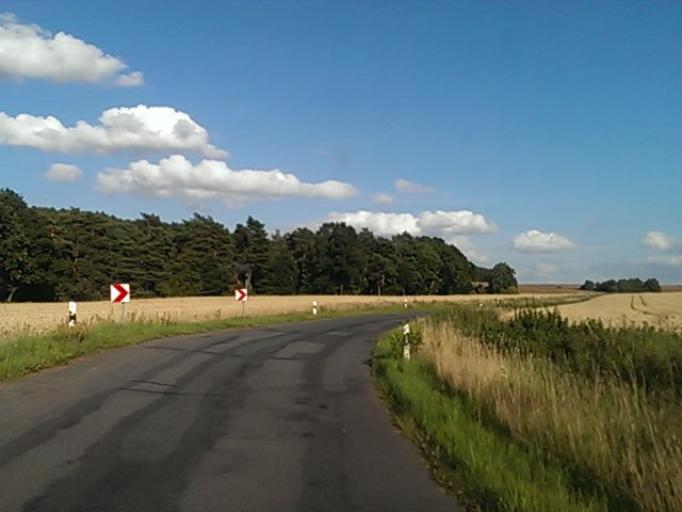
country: DE
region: Brandenburg
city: Niemegk
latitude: 52.0258
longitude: 12.6447
